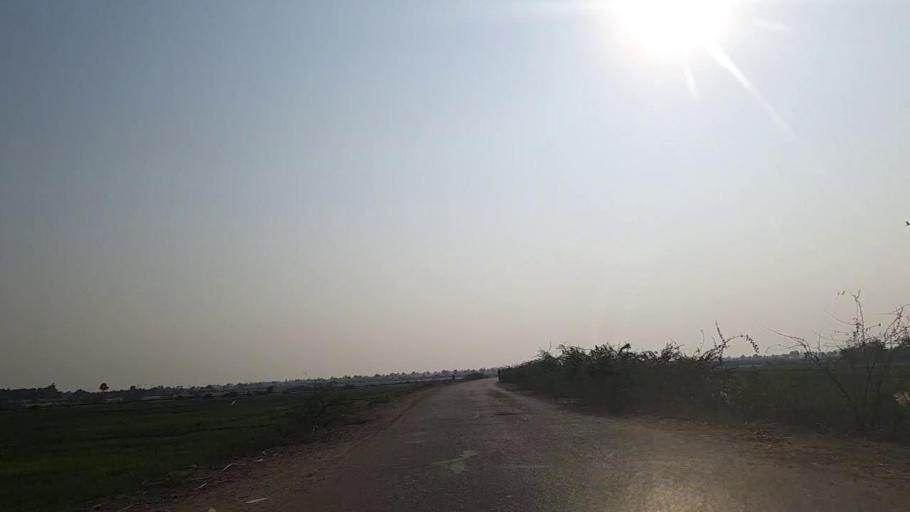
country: PK
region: Sindh
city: Jam Sahib
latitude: 26.2902
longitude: 68.6264
